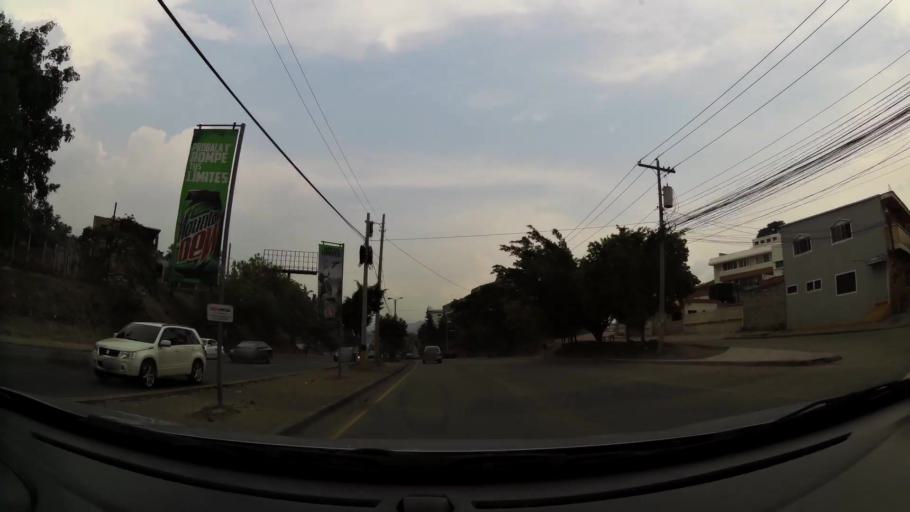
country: HN
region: Francisco Morazan
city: Tegucigalpa
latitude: 14.0788
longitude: -87.2164
